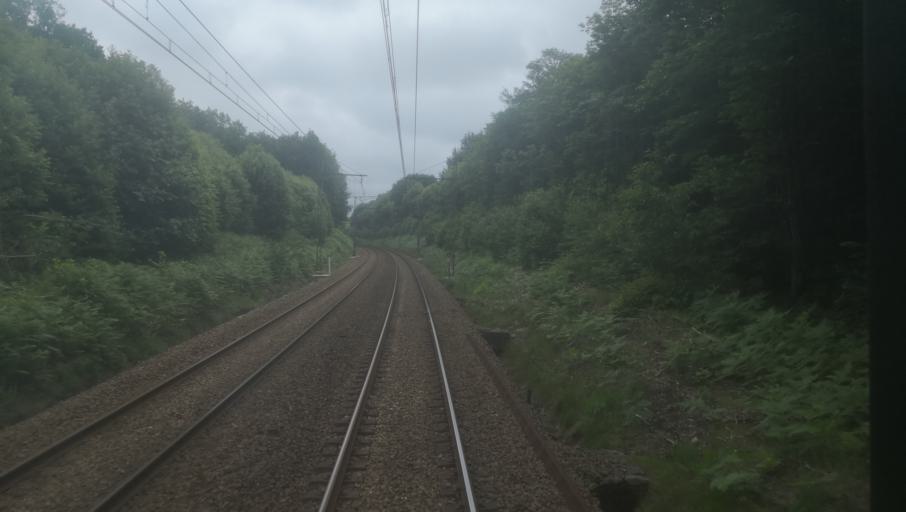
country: FR
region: Limousin
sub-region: Departement de la Haute-Vienne
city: Ambazac
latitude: 45.9682
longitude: 1.4567
